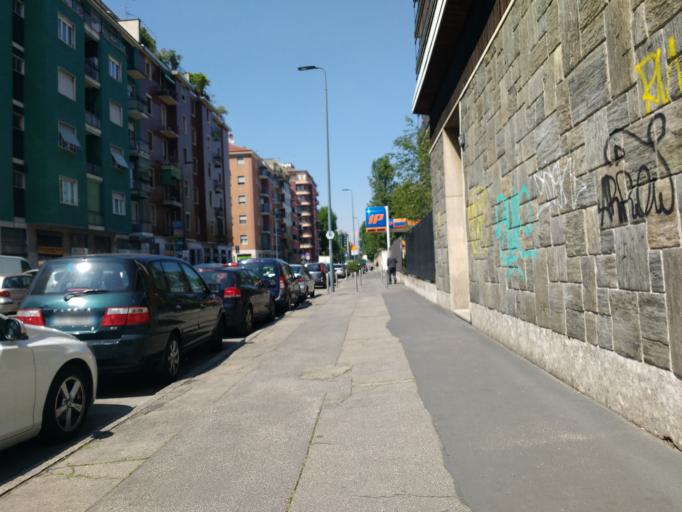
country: IT
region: Lombardy
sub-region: Citta metropolitana di Milano
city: Linate
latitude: 45.4649
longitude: 9.2353
